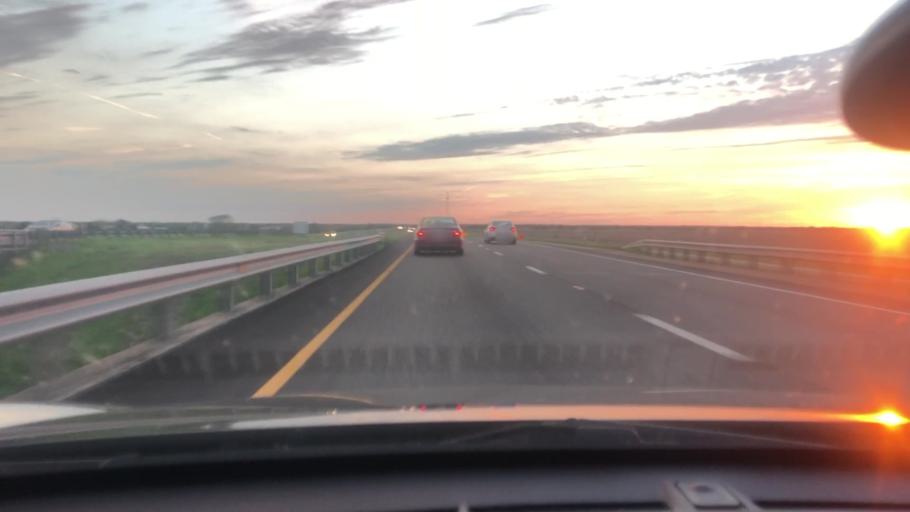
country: US
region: Texas
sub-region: Victoria County
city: Inez
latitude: 28.9342
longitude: -96.7350
